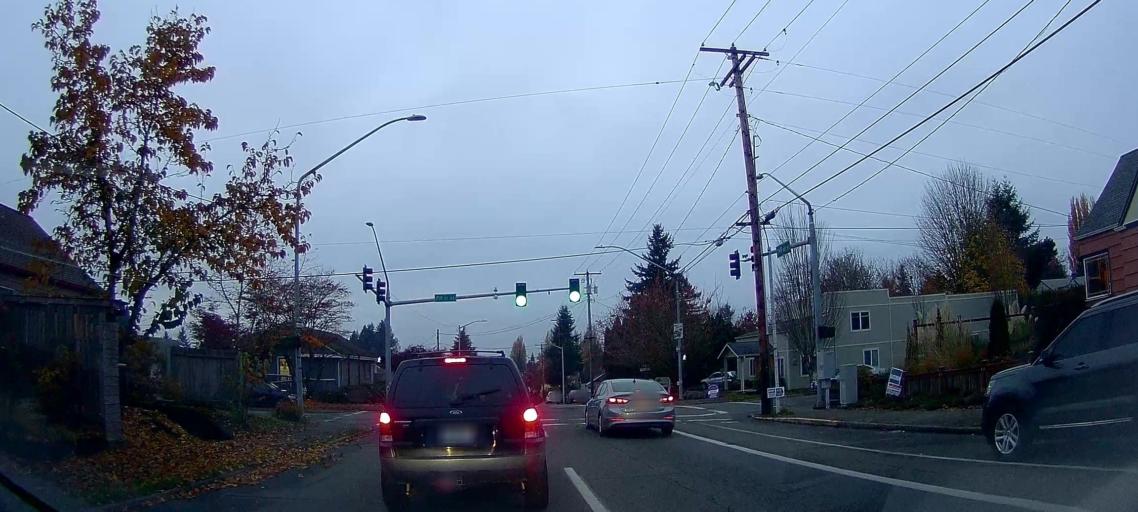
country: US
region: Washington
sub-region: Thurston County
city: Olympia
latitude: 47.0469
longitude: -122.8772
